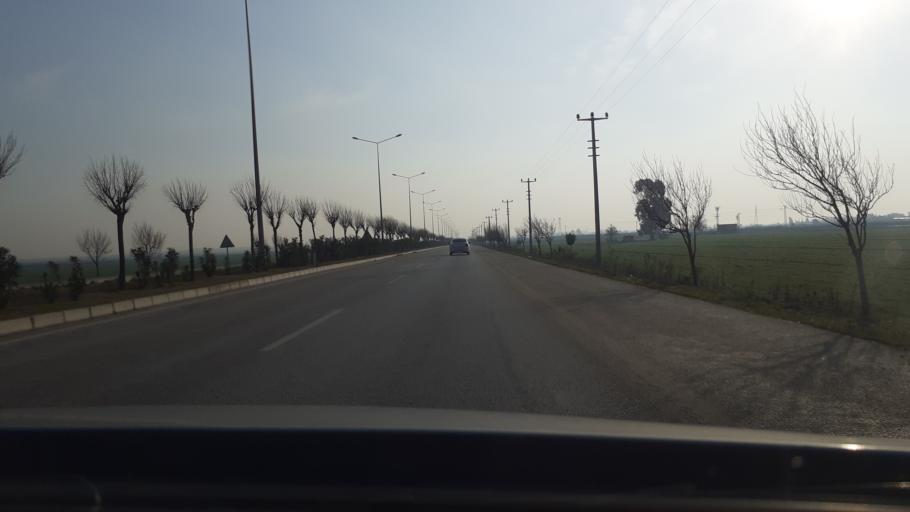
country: TR
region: Hatay
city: Serinyol
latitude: 36.3718
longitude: 36.2338
